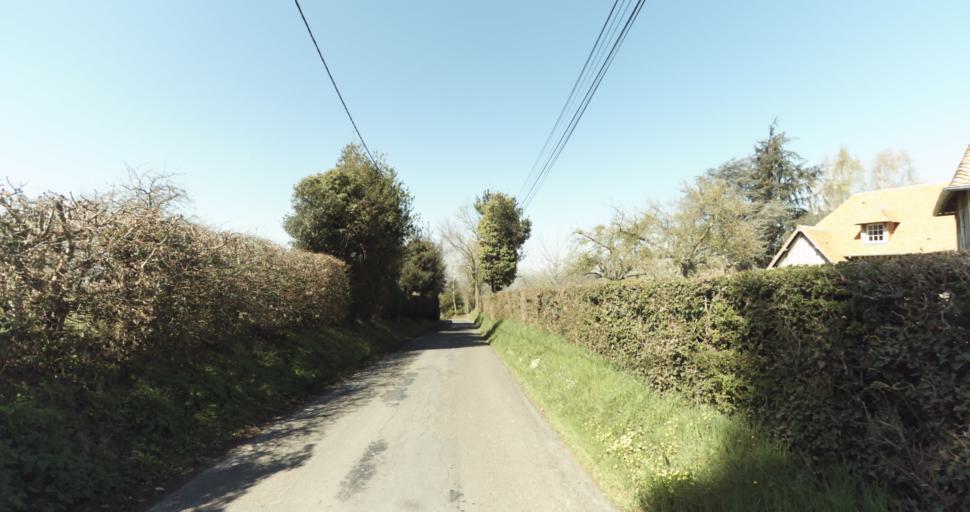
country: FR
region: Lower Normandy
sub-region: Departement du Calvados
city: Saint-Pierre-sur-Dives
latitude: 49.0172
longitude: 0.0563
